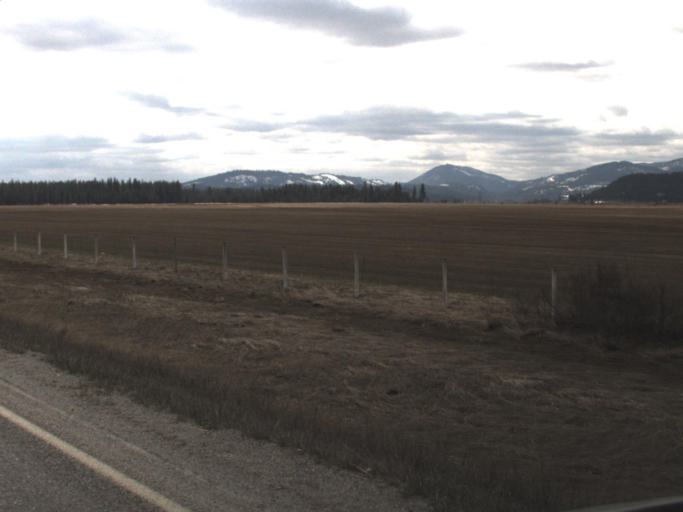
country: US
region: Washington
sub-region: Pend Oreille County
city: Newport
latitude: 48.3263
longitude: -117.2980
